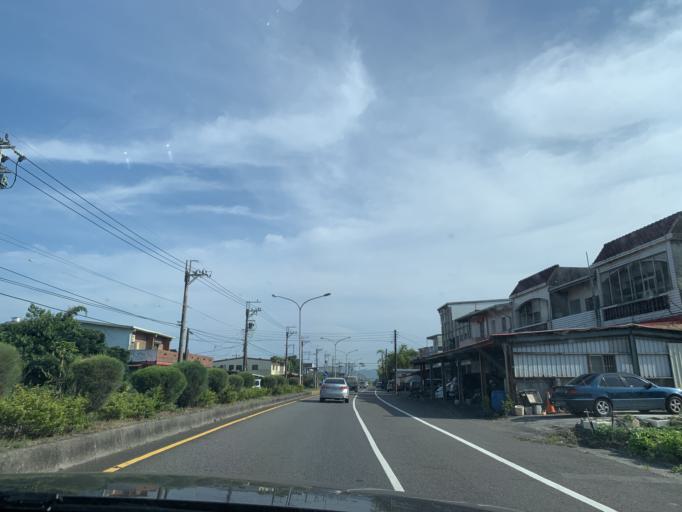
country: TW
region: Taiwan
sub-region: Yilan
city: Yilan
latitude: 24.7481
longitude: 121.8161
